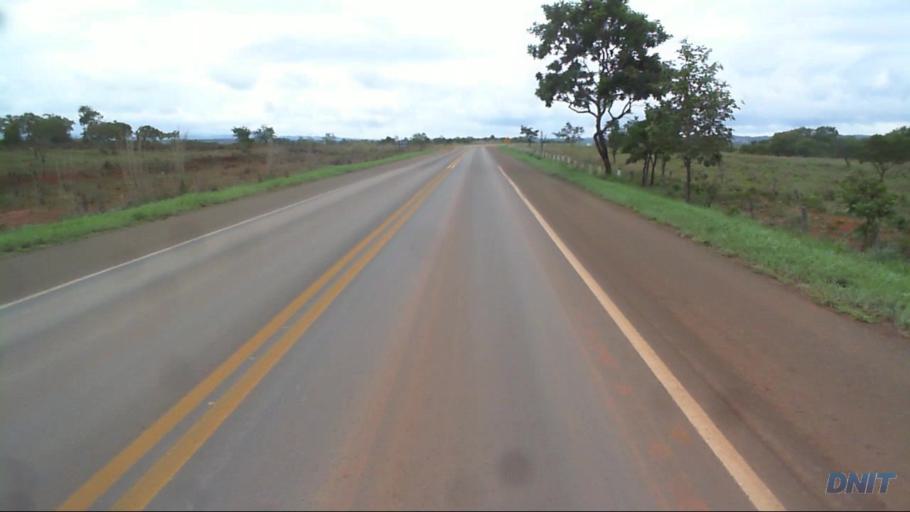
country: BR
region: Goias
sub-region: Padre Bernardo
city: Padre Bernardo
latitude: -15.1502
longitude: -48.3419
